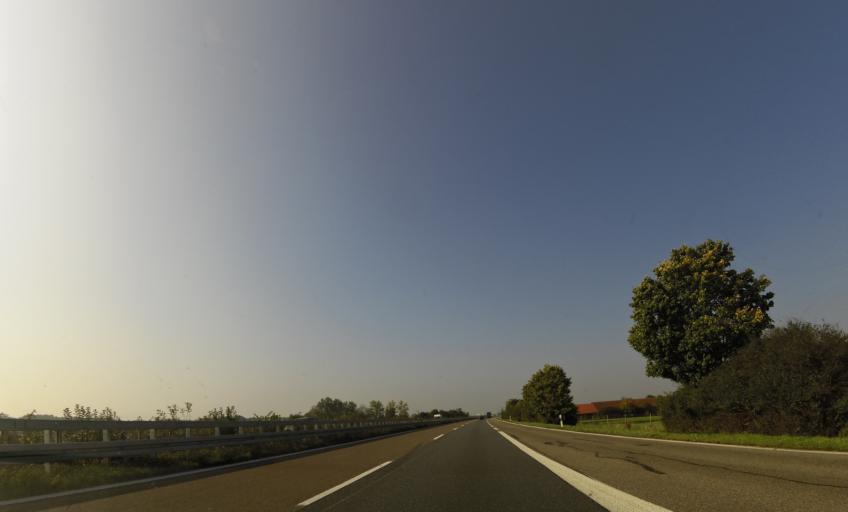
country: DE
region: Baden-Wuerttemberg
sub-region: Regierungsbezirk Stuttgart
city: Satteldorf
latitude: 49.1890
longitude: 10.1060
